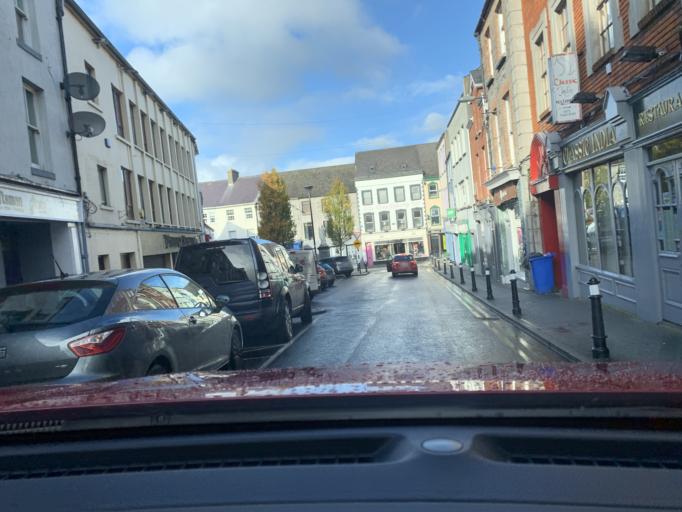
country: IE
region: Connaught
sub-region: Sligo
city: Sligo
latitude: 54.2700
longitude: -8.4734
